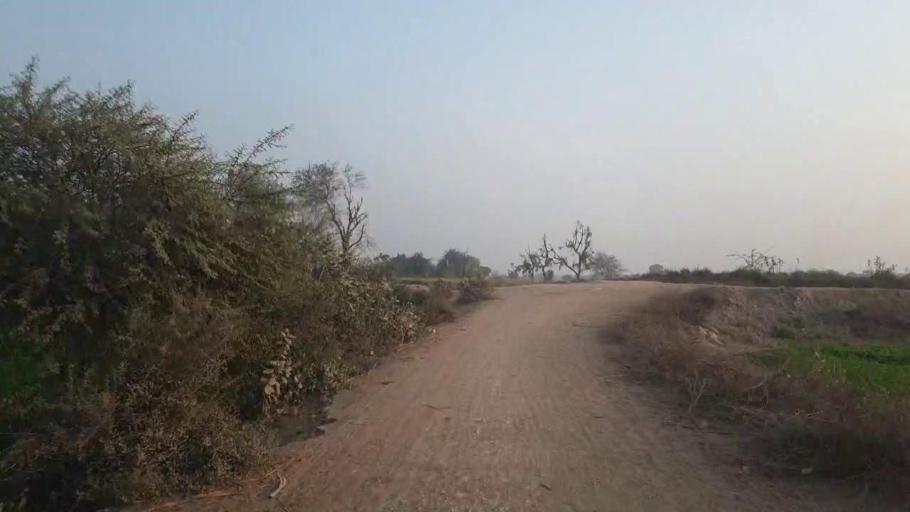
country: PK
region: Sindh
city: Bhit Shah
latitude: 25.7676
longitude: 68.4603
